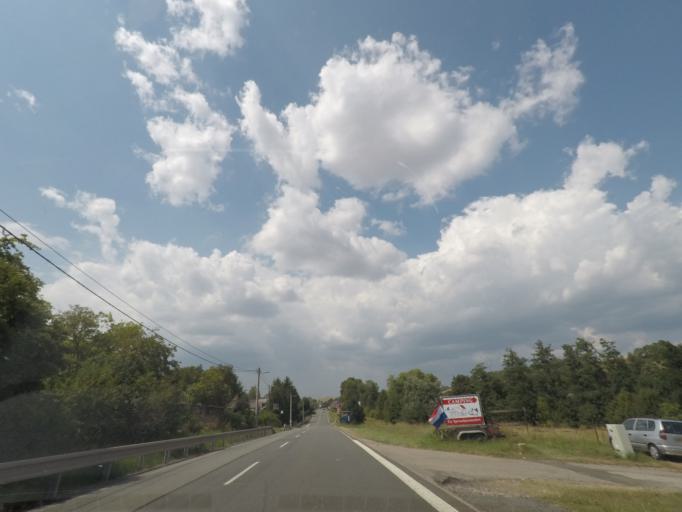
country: CZ
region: Kralovehradecky
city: Zadni Mostek
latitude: 50.5384
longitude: 15.6555
